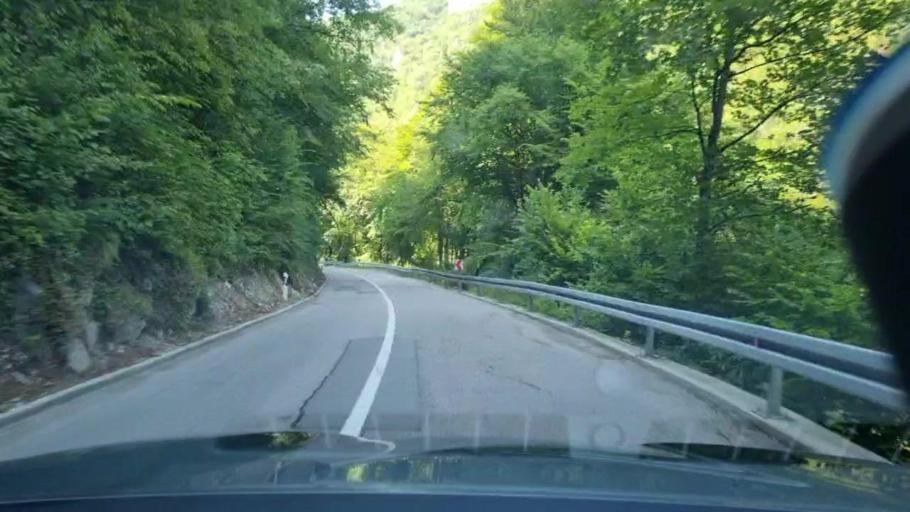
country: BA
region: Federation of Bosnia and Herzegovina
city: Stijena
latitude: 44.8797
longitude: 16.0703
